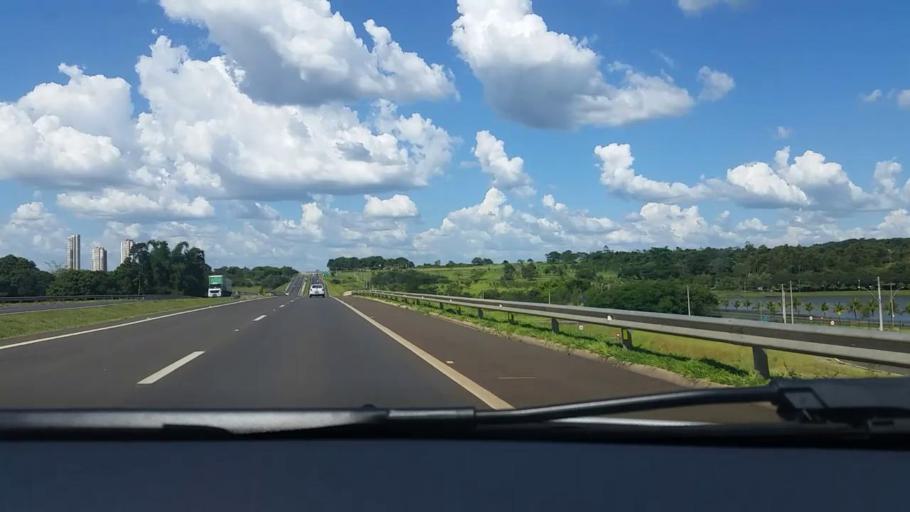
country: BR
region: Sao Paulo
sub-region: Bauru
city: Bauru
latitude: -22.3868
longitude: -49.0727
